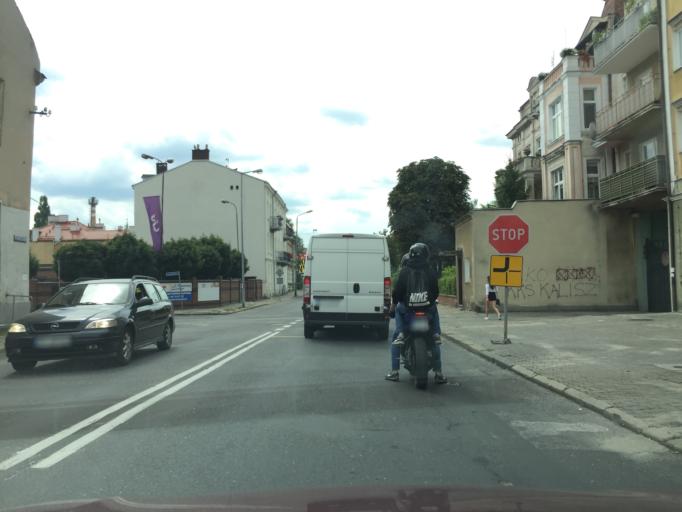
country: PL
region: Greater Poland Voivodeship
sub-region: Kalisz
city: Kalisz
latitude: 51.7677
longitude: 18.0966
